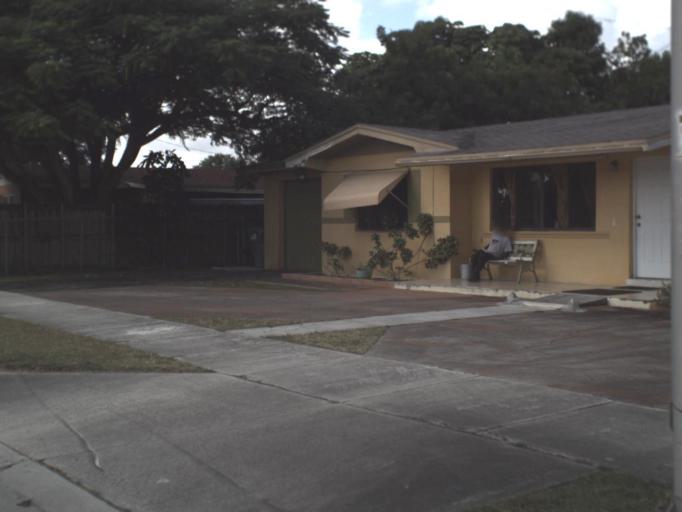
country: US
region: Florida
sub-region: Miami-Dade County
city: Leisure City
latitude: 25.4996
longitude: -80.4281
